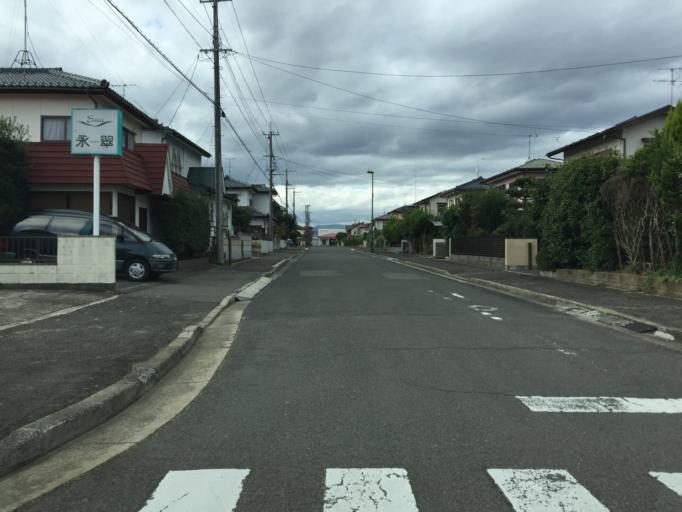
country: JP
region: Fukushima
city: Fukushima-shi
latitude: 37.7080
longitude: 140.4729
